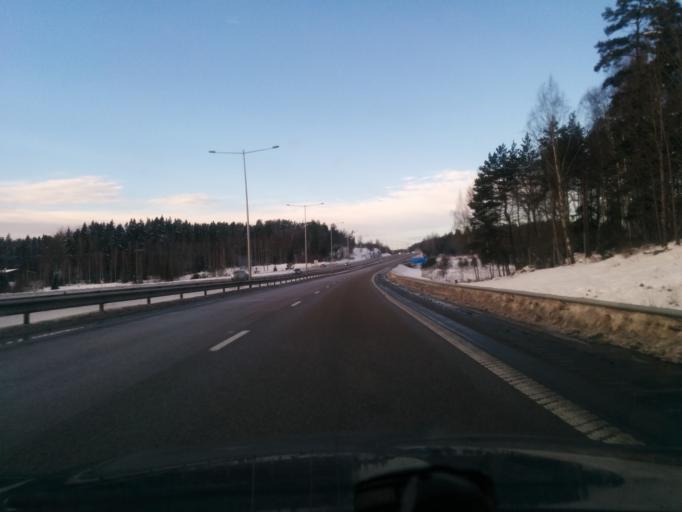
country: SE
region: Stockholm
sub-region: Upplands-Bro Kommun
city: Bro
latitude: 59.5294
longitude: 17.6345
